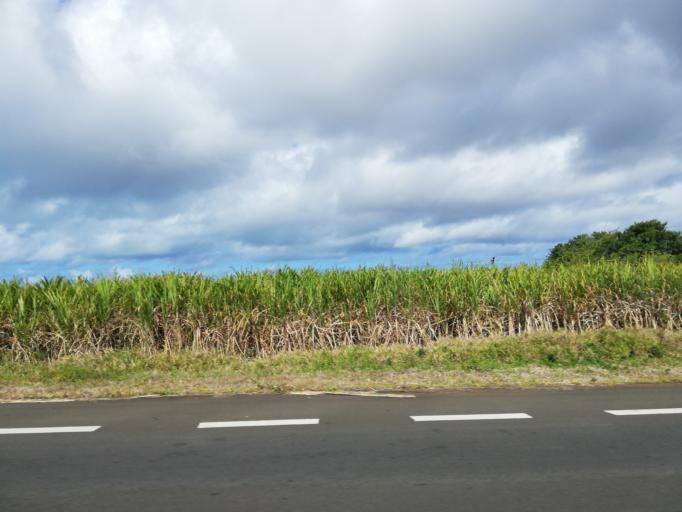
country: MU
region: Grand Port
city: Beau Vallon
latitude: -20.4049
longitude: 57.6763
